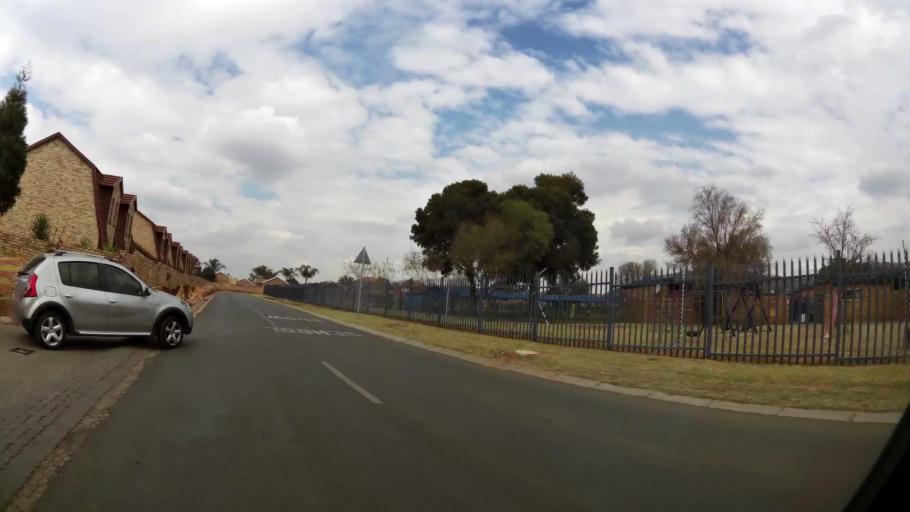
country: ZA
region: Gauteng
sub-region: West Rand District Municipality
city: Muldersdriseloop
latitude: -26.0929
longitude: 27.8770
